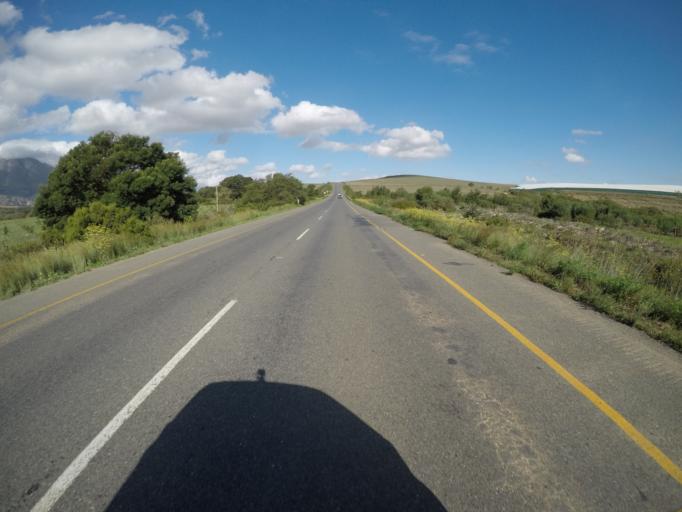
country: ZA
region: Western Cape
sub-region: Overberg District Municipality
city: Swellendam
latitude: -33.9635
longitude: 20.2440
